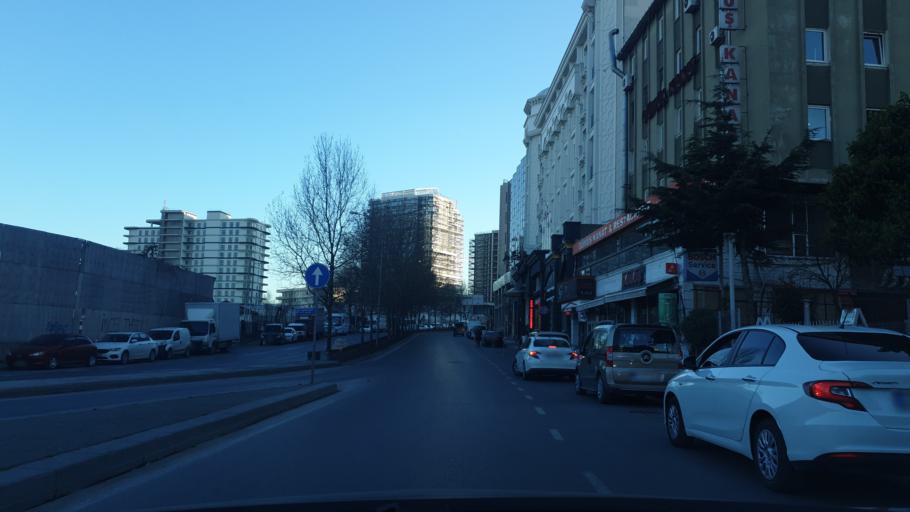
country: TR
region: Istanbul
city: merter keresteciler
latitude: 41.0146
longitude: 28.8780
